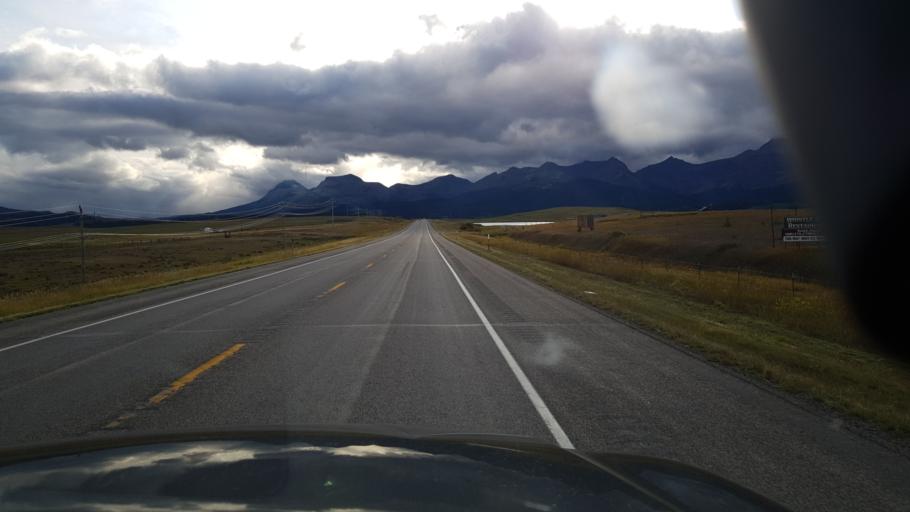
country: US
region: Montana
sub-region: Glacier County
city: South Browning
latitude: 48.4576
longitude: -113.1807
